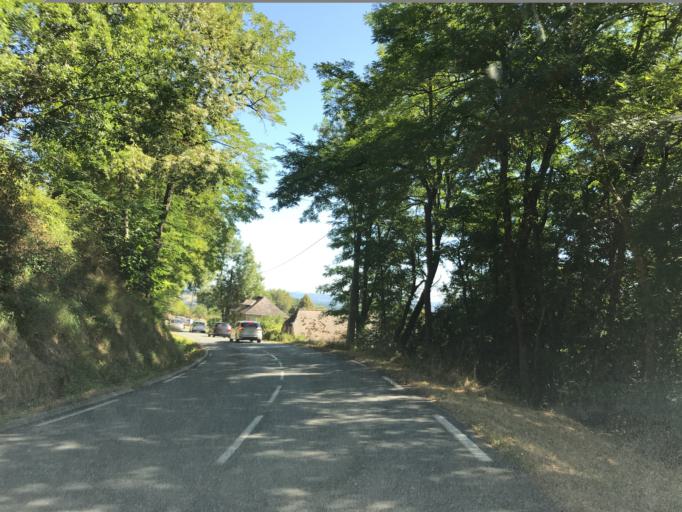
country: FR
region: Limousin
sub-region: Departement de la Correze
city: Larche
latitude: 45.1073
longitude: 1.3873
